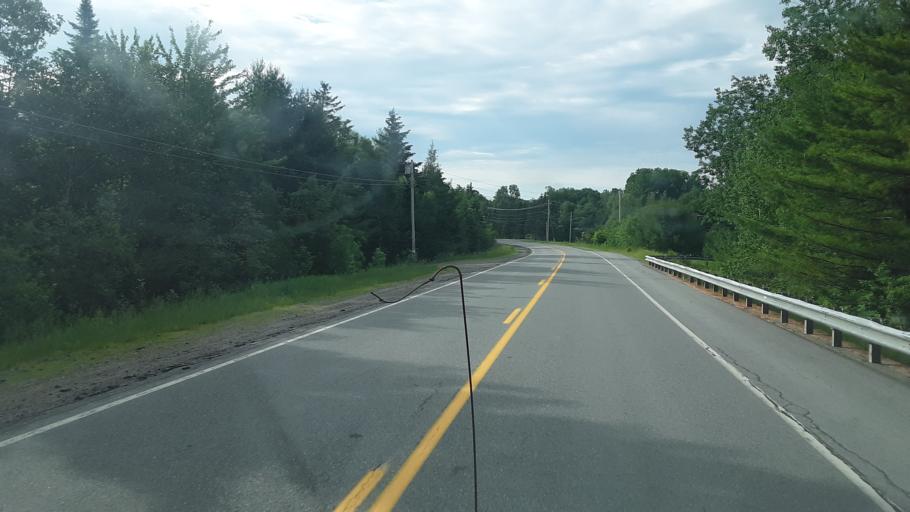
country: US
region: Maine
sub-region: Penobscot County
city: Medway
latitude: 45.6033
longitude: -68.5196
